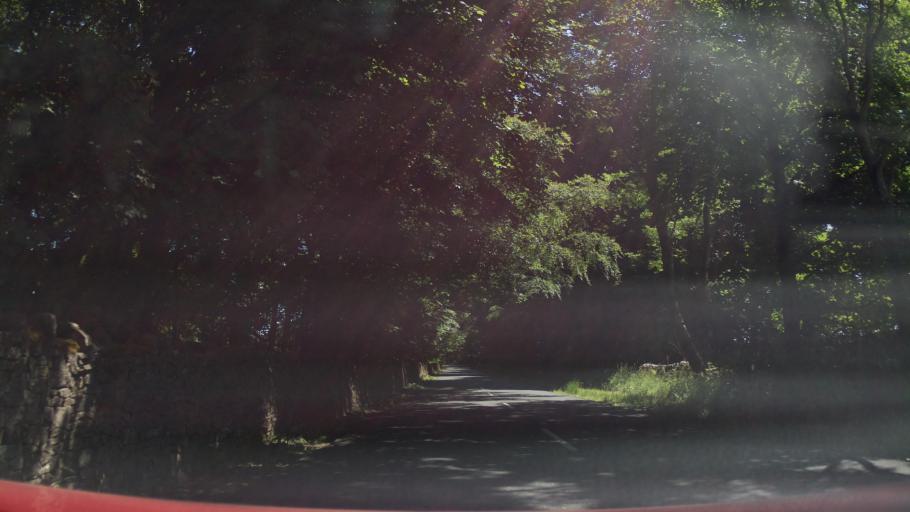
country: GB
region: England
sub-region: Derbyshire
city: Tideswell
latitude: 53.2738
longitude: -1.8287
